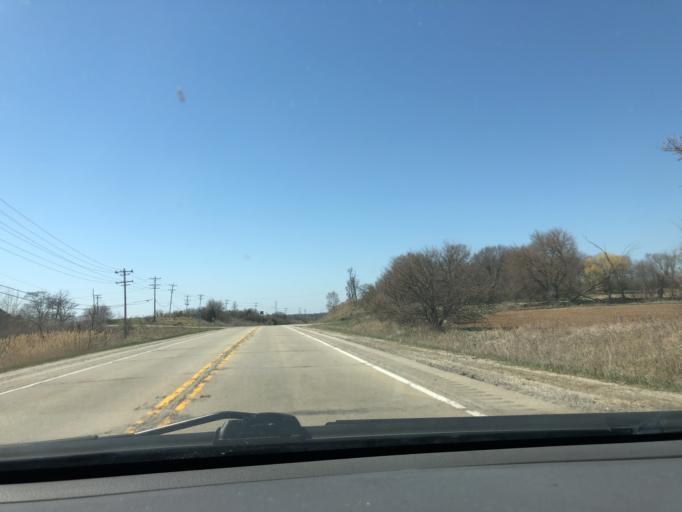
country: US
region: Illinois
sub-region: Kane County
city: Hampshire
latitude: 42.1379
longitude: -88.5030
